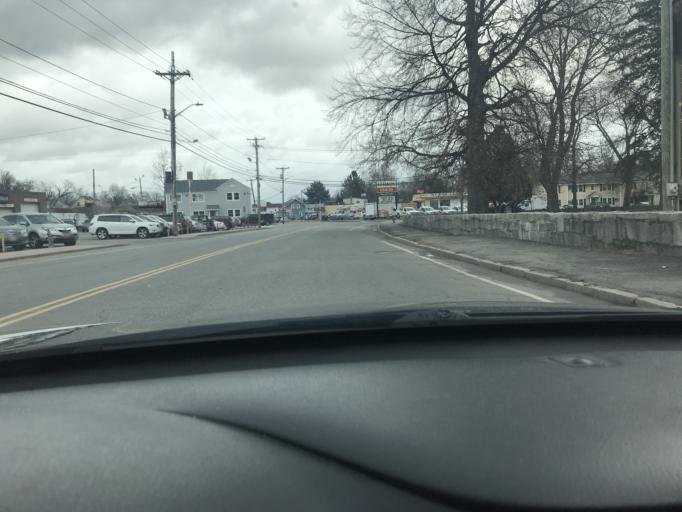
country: US
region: Massachusetts
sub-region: Middlesex County
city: Lowell
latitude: 42.6359
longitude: -71.3507
